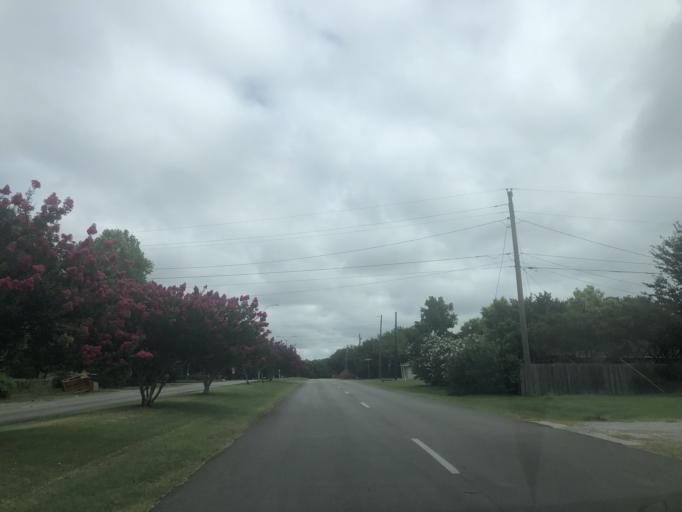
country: US
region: Texas
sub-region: Dallas County
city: Duncanville
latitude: 32.6620
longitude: -96.9170
